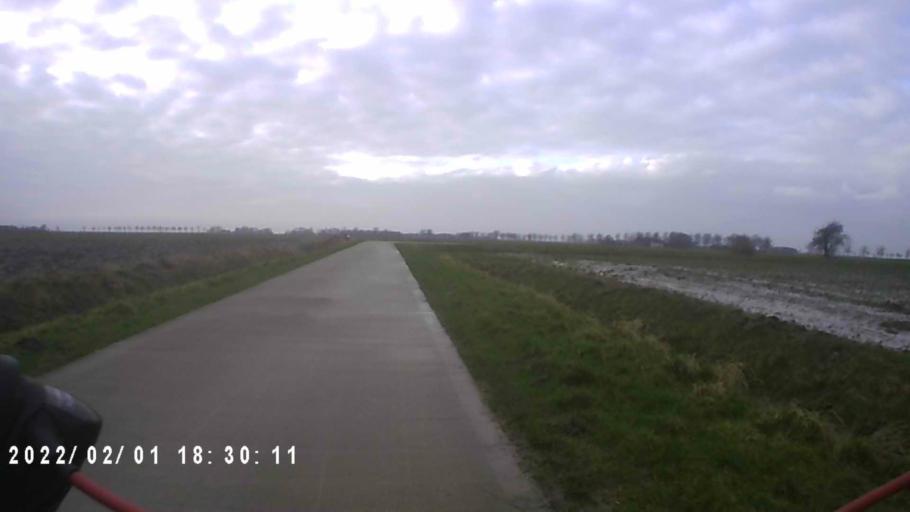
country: NL
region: Groningen
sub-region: Gemeente De Marne
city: Ulrum
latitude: 53.3559
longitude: 6.3198
